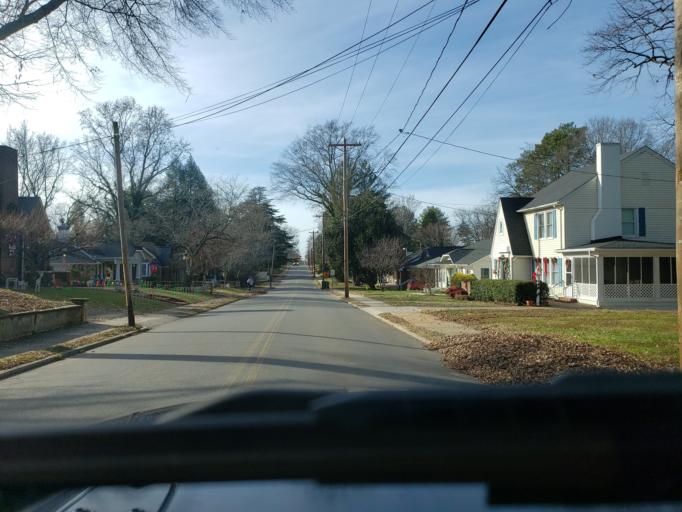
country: US
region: North Carolina
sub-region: Cleveland County
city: Kings Mountain
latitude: 35.2381
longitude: -81.3497
